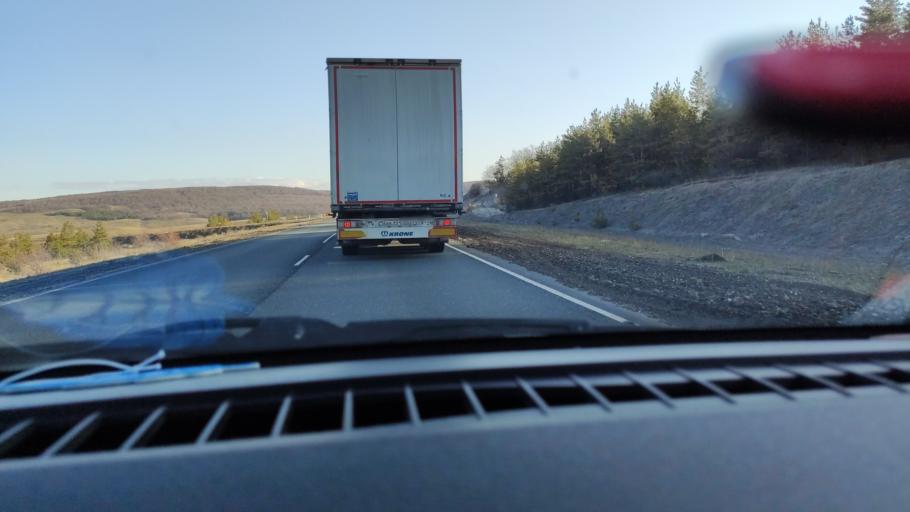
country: RU
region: Saratov
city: Alekseyevka
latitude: 52.3874
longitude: 47.9749
